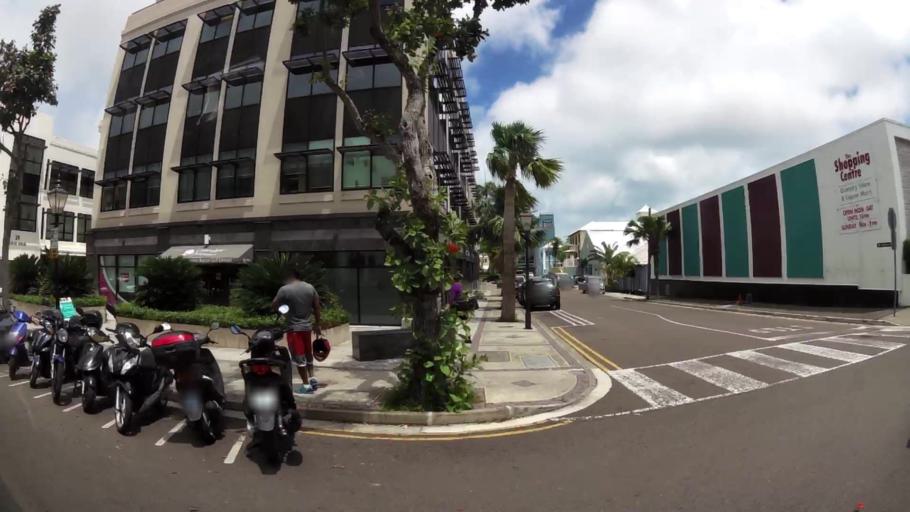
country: BM
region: Hamilton city
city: Hamilton
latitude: 32.2951
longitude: -64.7833
